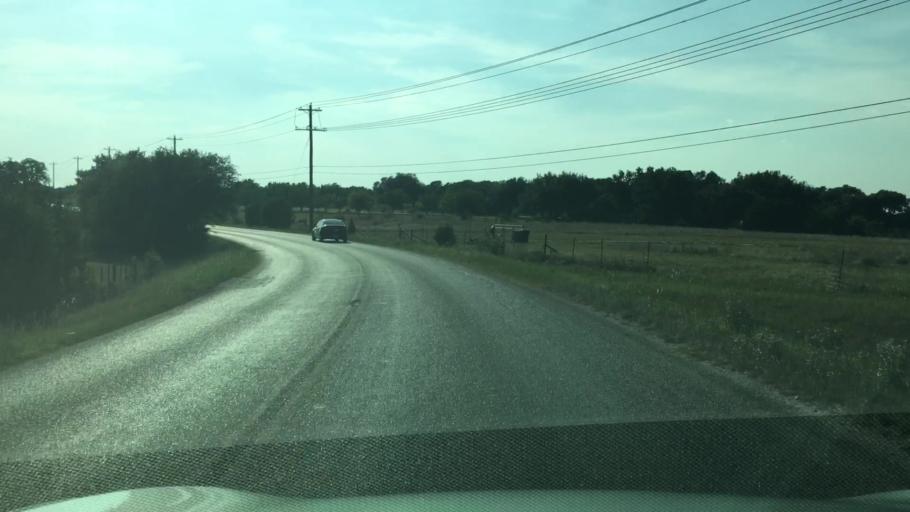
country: US
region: Texas
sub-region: Hays County
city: Dripping Springs
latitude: 30.1536
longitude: -97.9949
